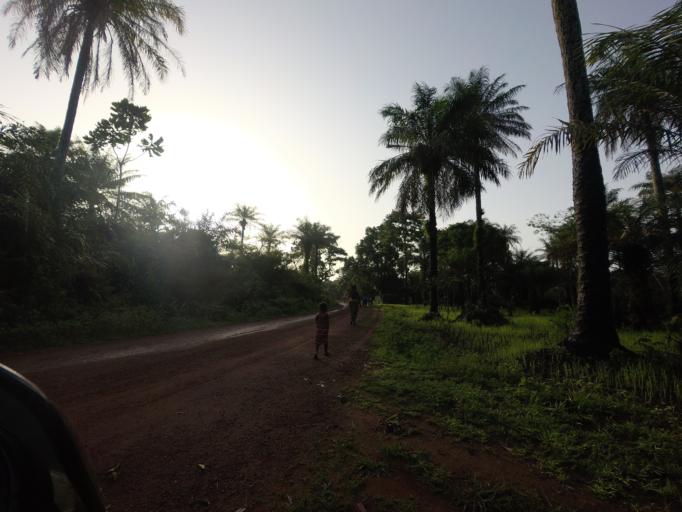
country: SL
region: Northern Province
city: Kambia
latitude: 9.0920
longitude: -12.9054
